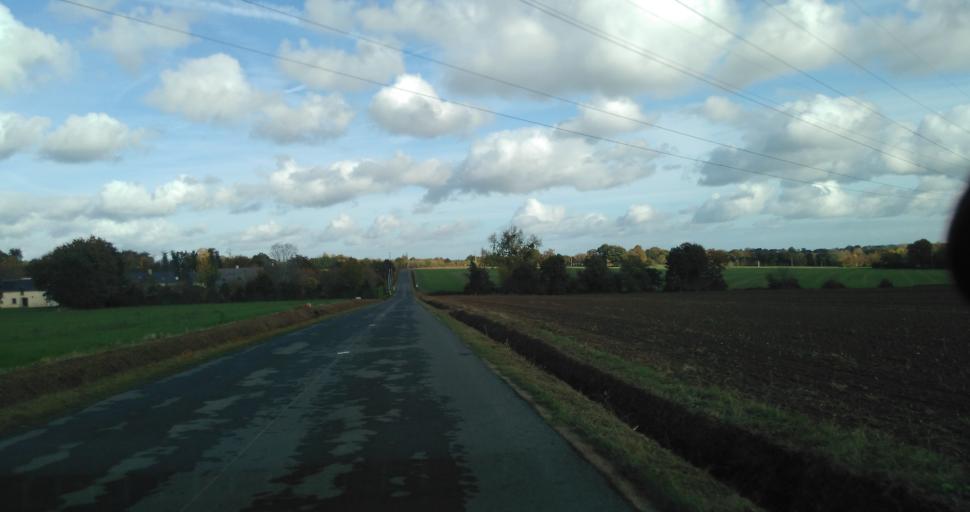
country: FR
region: Brittany
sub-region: Departement d'Ille-et-Vilaine
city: Boisgervilly
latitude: 48.1488
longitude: -2.0784
